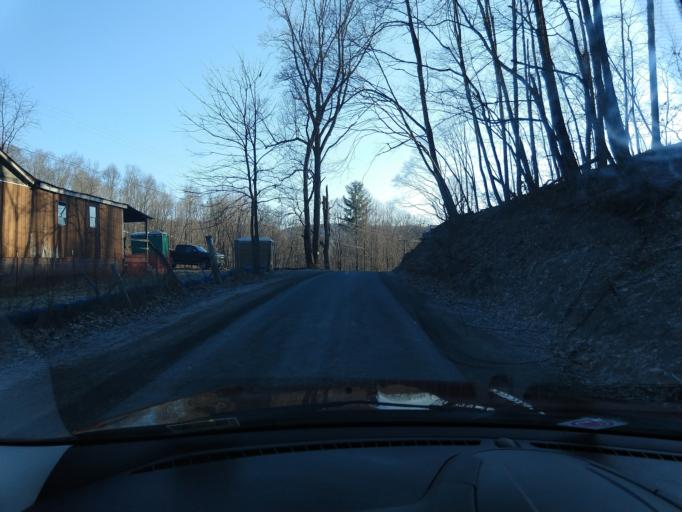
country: US
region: West Virginia
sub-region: Greenbrier County
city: Rainelle
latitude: 37.9234
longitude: -80.7399
